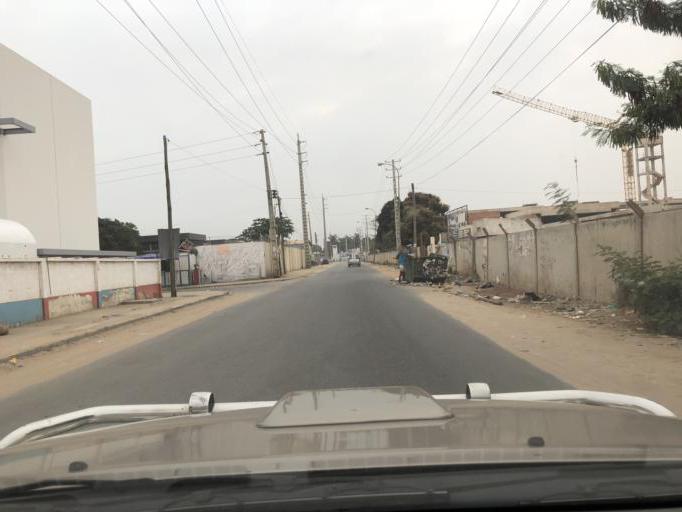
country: AO
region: Luanda
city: Luanda
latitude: -8.8897
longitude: 13.1893
